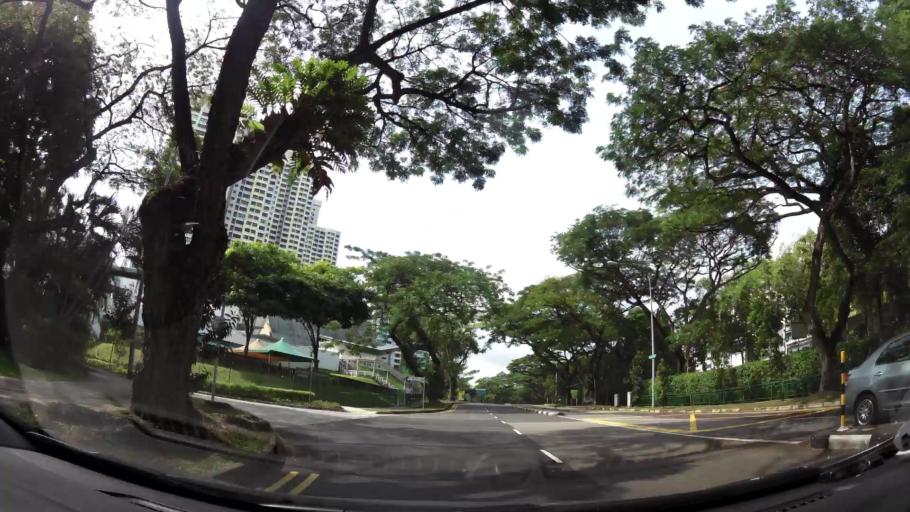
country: SG
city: Singapore
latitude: 1.3077
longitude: 103.7825
